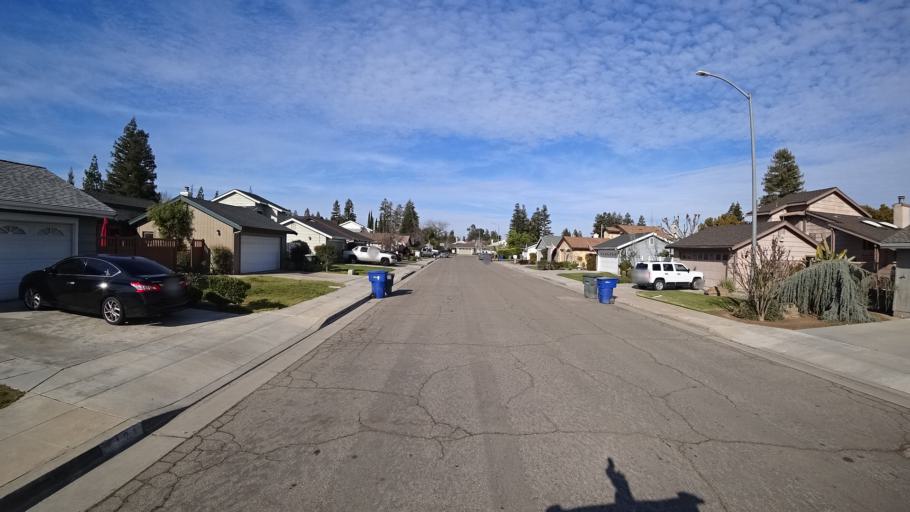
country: US
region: California
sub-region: Fresno County
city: West Park
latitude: 36.8343
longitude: -119.8652
